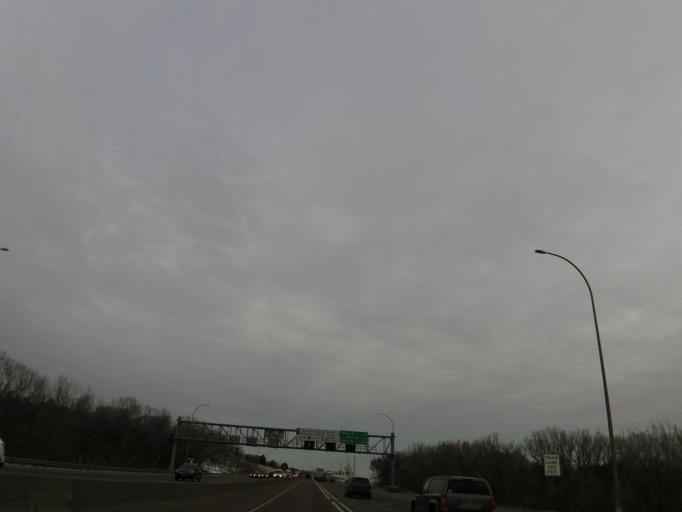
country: US
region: Minnesota
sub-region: Hennepin County
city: Bloomington
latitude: 44.8040
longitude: -93.2906
